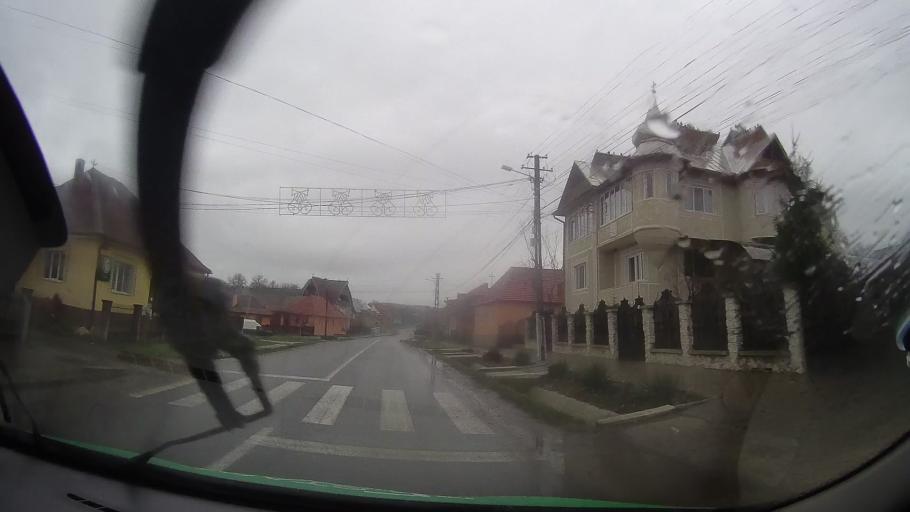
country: RO
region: Bistrita-Nasaud
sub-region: Comuna Monor
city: Monor
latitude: 46.9504
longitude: 24.6894
